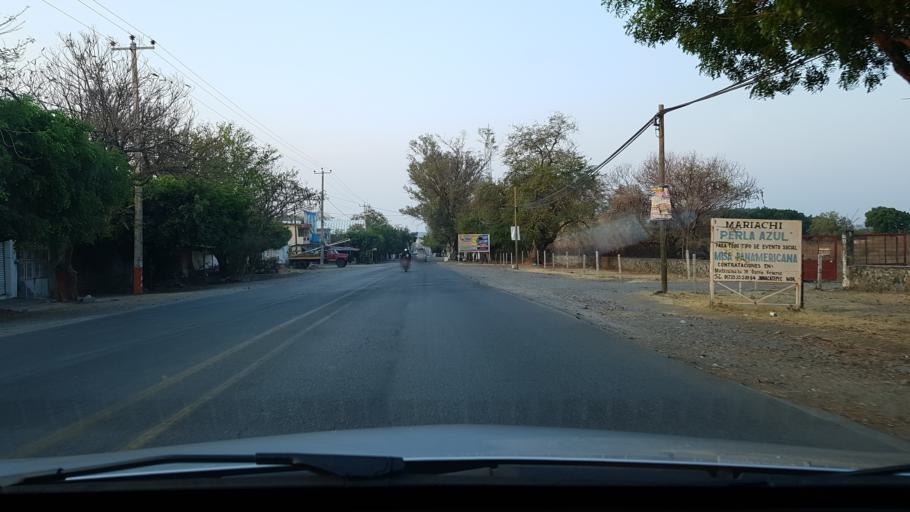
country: MX
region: Morelos
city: Jonacatepec de Leandro Valle
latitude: 18.6893
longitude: -98.8022
